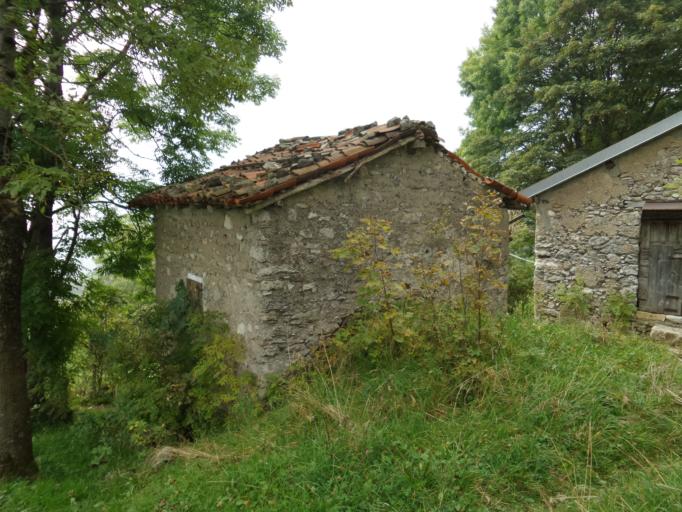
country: IT
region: Lombardy
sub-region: Provincia di Lecco
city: Ballabio
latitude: 45.9062
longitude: 9.4008
